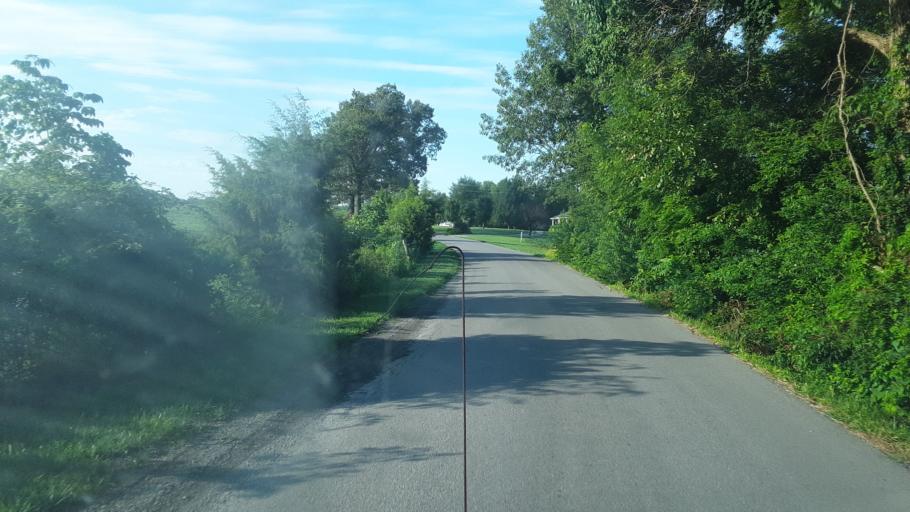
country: US
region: Kentucky
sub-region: Todd County
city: Elkton
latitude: 36.7375
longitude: -87.1679
